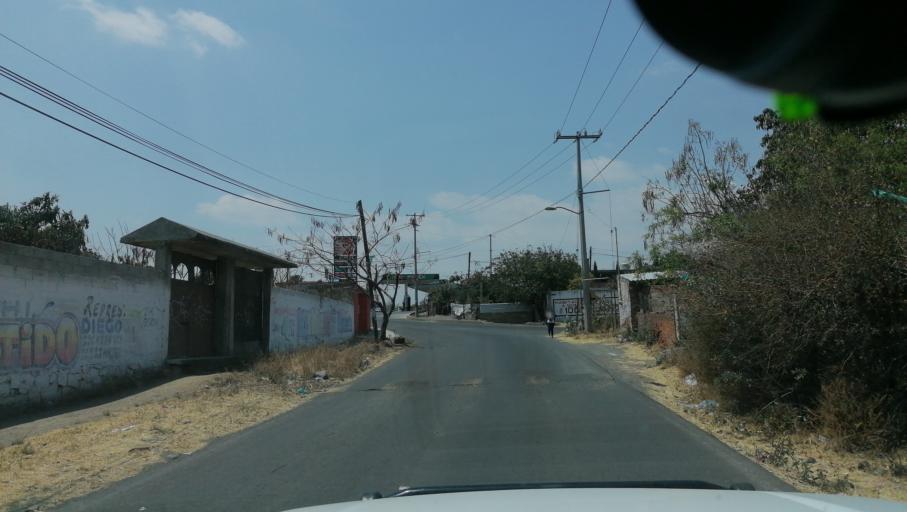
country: MX
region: Puebla
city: Atlixco
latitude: 18.9108
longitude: -98.4728
